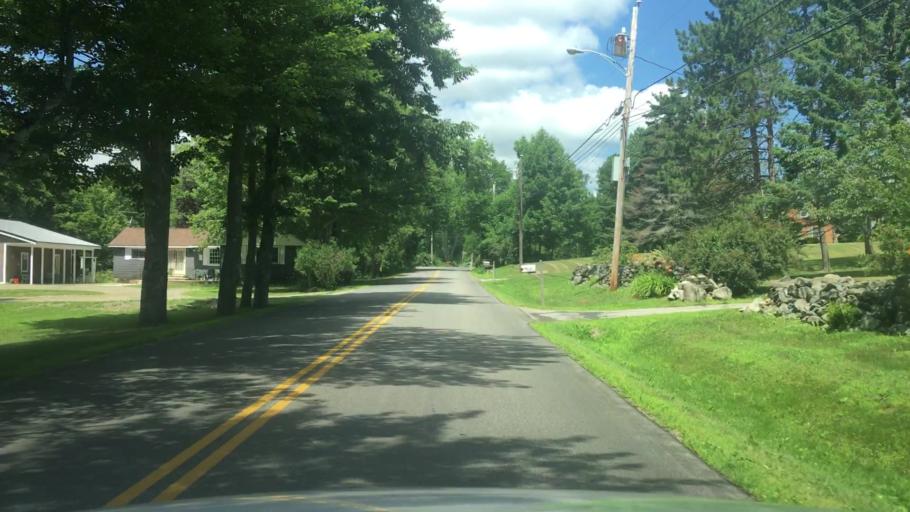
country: US
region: Maine
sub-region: Waldo County
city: Belfast
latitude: 44.4160
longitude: -69.0418
